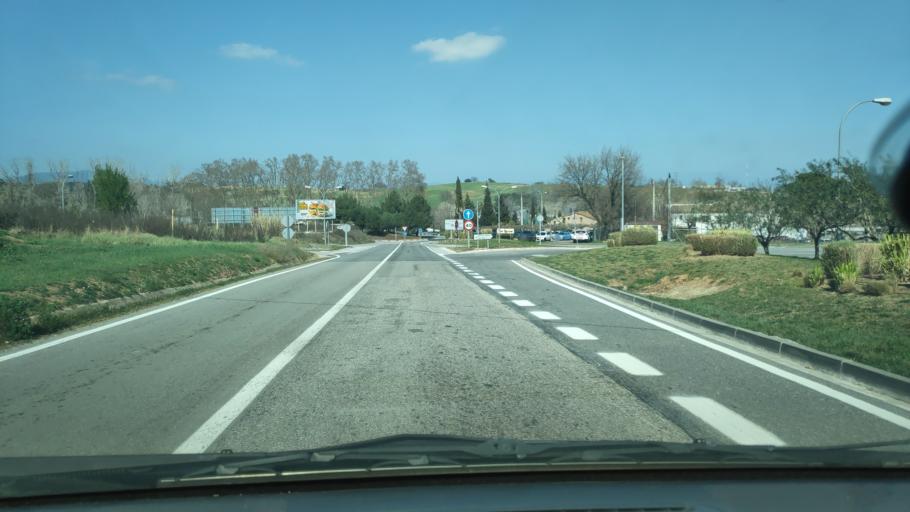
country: ES
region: Catalonia
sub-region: Provincia de Barcelona
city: Polinya
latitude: 41.5317
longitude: 2.1530
